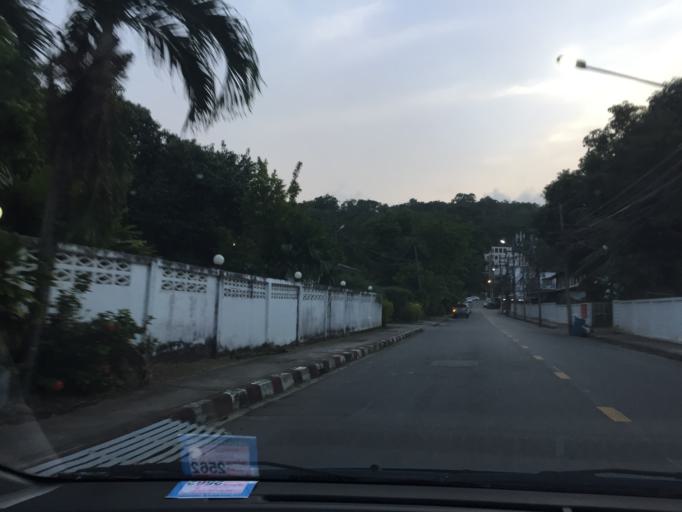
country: TH
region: Phuket
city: Wichit
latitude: 7.8940
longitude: 98.3871
